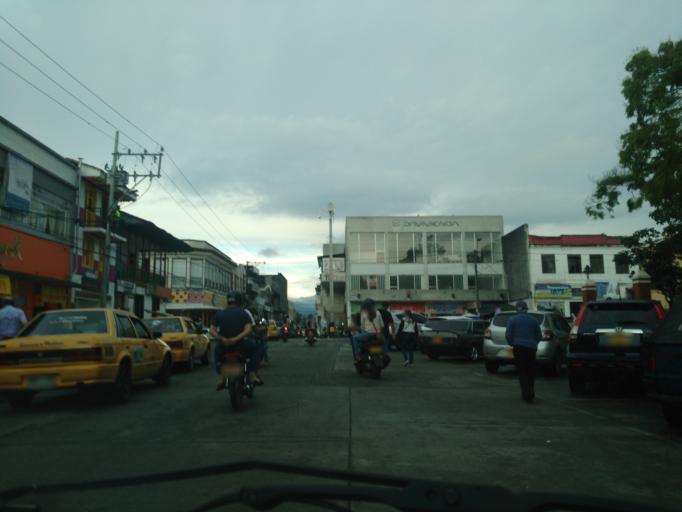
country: CO
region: Valle del Cauca
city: Sevilla
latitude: 4.2644
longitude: -75.9341
